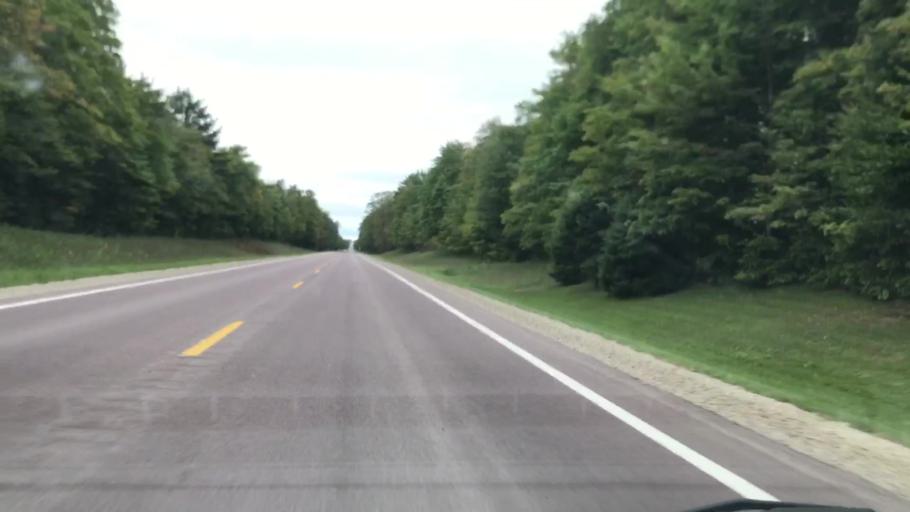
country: US
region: Michigan
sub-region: Luce County
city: Newberry
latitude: 46.2520
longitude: -85.5725
